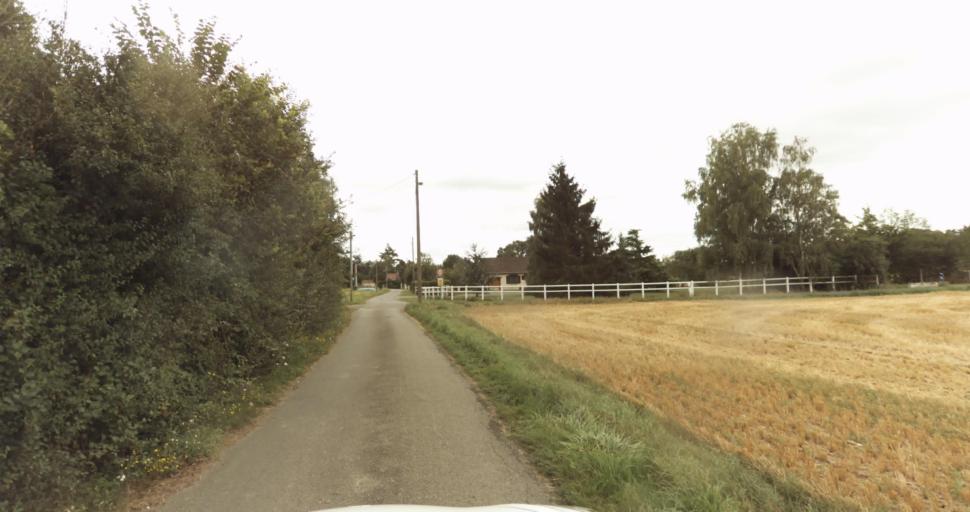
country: FR
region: Haute-Normandie
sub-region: Departement de l'Eure
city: La Madeleine-de-Nonancourt
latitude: 48.8416
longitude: 1.2088
